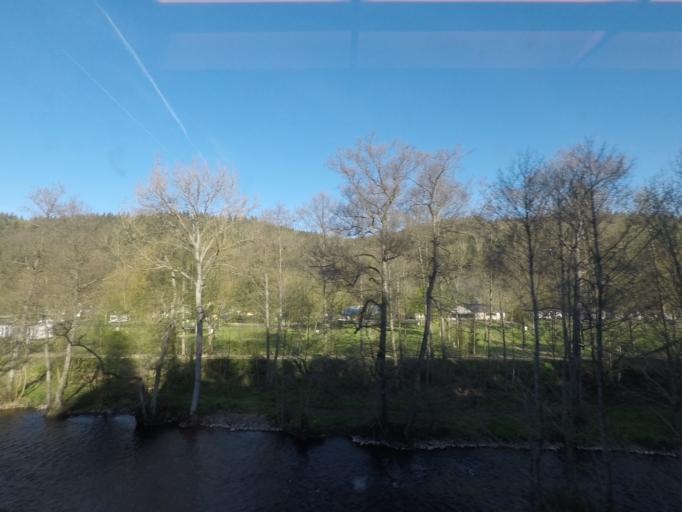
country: BE
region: Wallonia
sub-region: Province du Luxembourg
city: Nassogne
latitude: 50.0989
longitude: 5.2904
